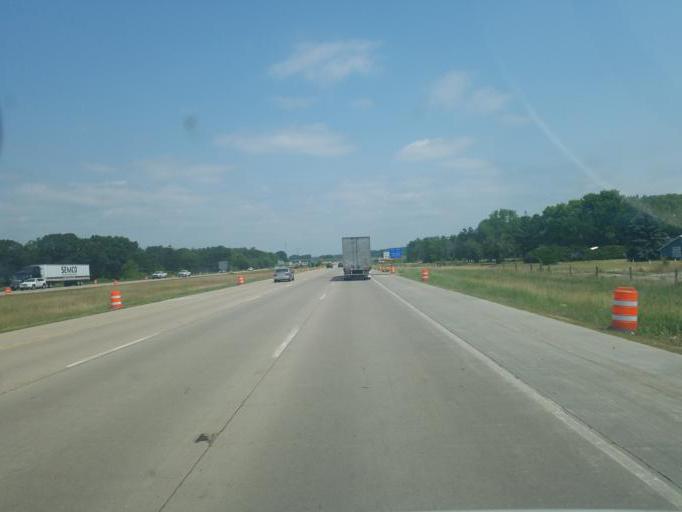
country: US
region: Wisconsin
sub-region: Columbia County
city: Poynette
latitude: 43.4007
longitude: -89.4666
